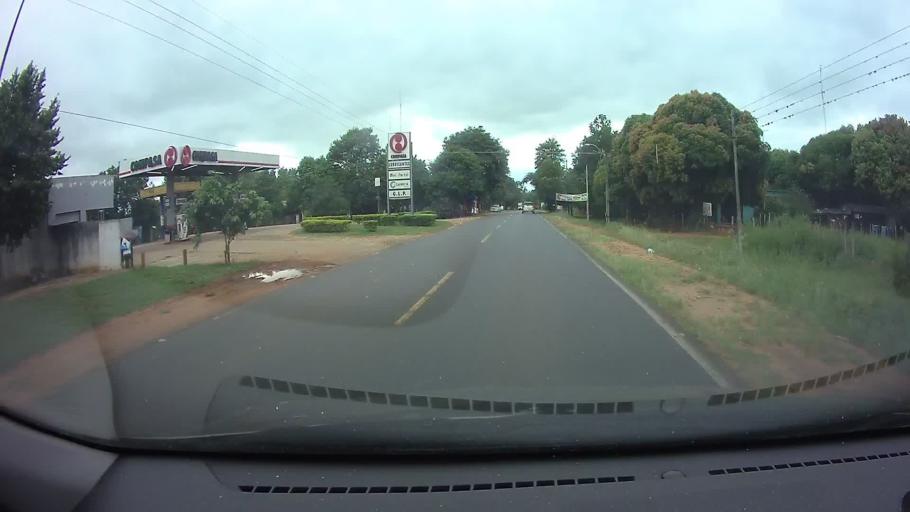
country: PY
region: Central
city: Guarambare
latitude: -25.5426
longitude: -57.4998
